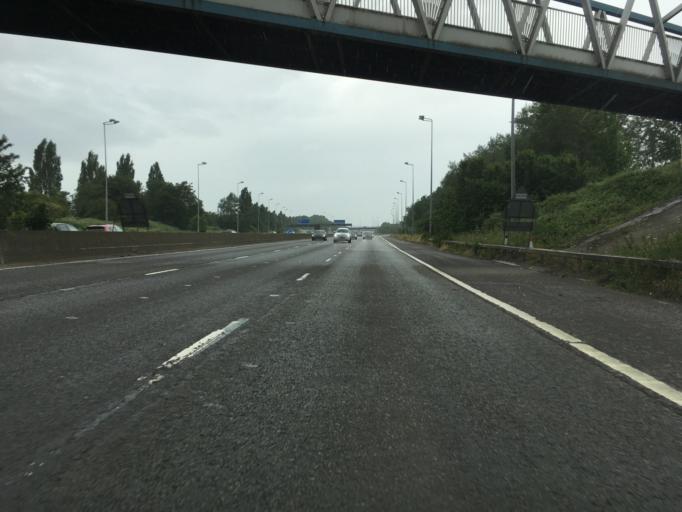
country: GB
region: England
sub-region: North Somerset
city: Easton-in-Gordano
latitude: 51.5088
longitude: -2.6606
